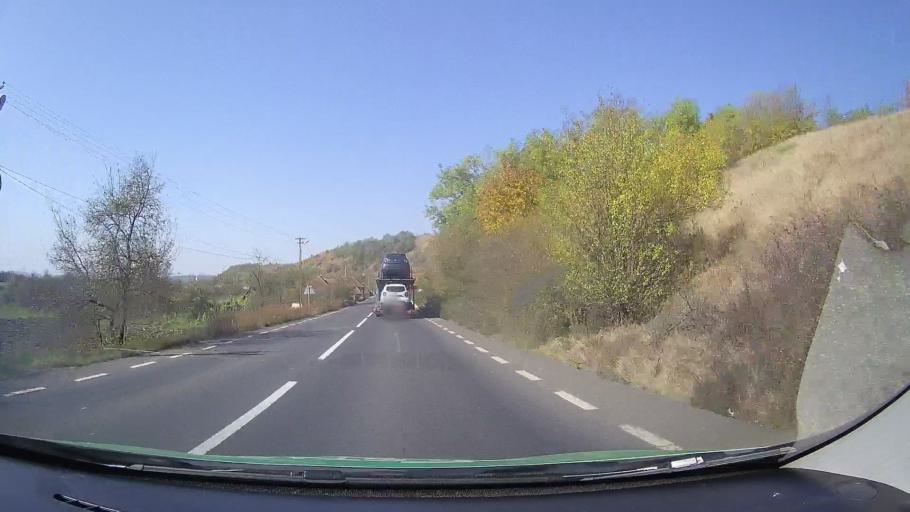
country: RO
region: Arad
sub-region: Comuna Varadia de Mures
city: Varadia de Mures
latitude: 46.0328
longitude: 22.1039
